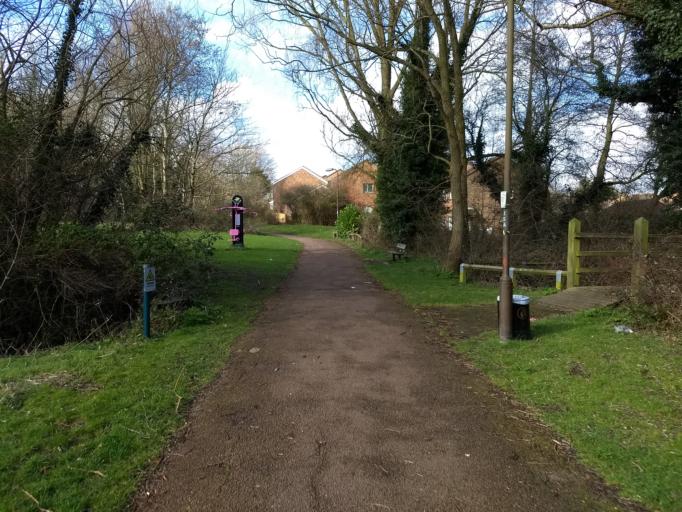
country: GB
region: England
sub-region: Milton Keynes
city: Milton Keynes
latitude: 52.0306
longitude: -0.7389
